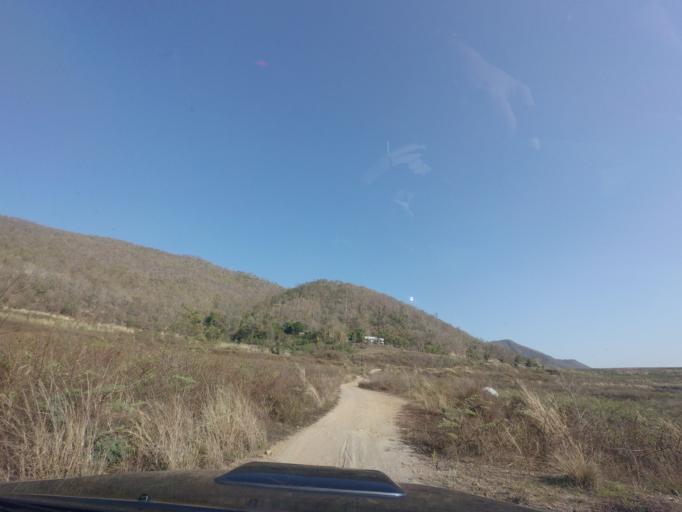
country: TH
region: Chiang Mai
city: San Sai
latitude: 18.9438
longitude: 99.1372
